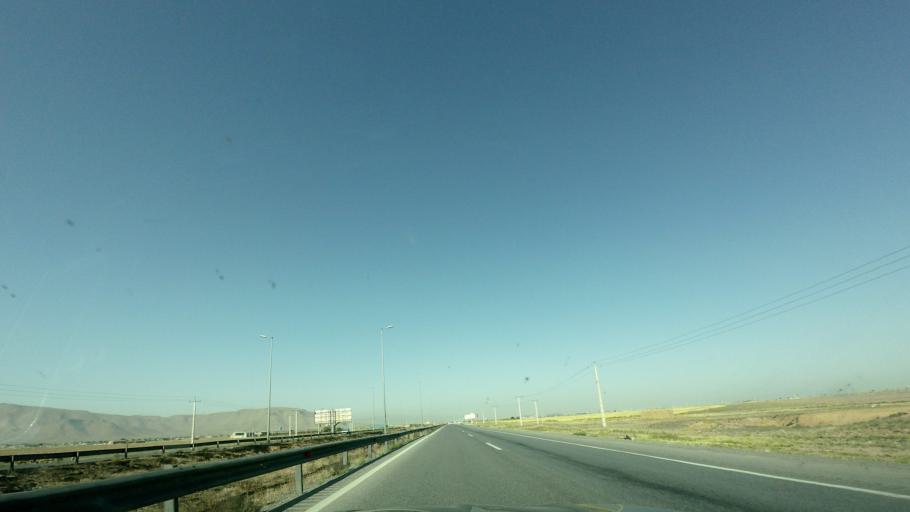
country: IR
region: Markazi
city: Arak
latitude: 34.1627
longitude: 50.0206
